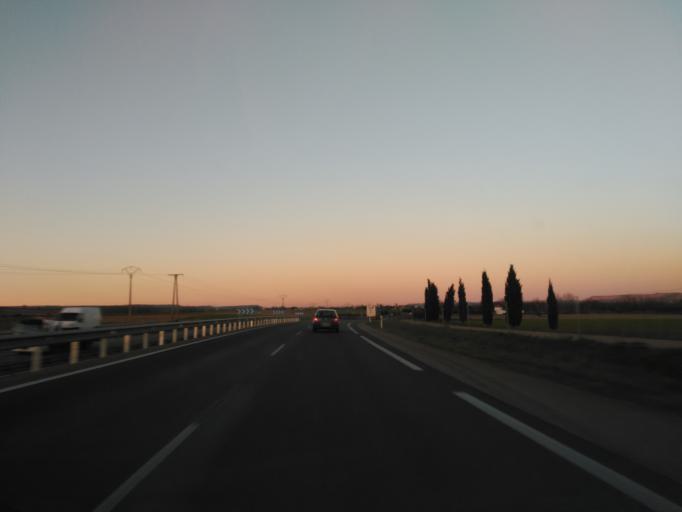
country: ES
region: Castille and Leon
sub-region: Provincia de Valladolid
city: Cubillas de Santa Marta
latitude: 41.7868
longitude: -4.6089
